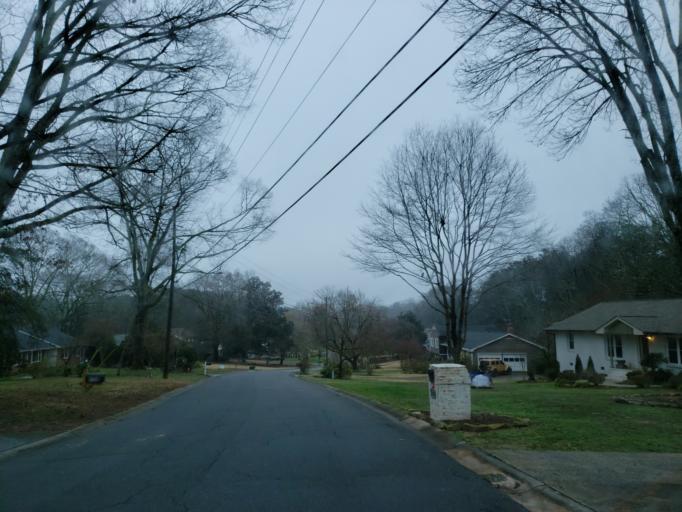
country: US
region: Georgia
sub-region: Cobb County
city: Fair Oaks
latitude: 33.9242
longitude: -84.5699
